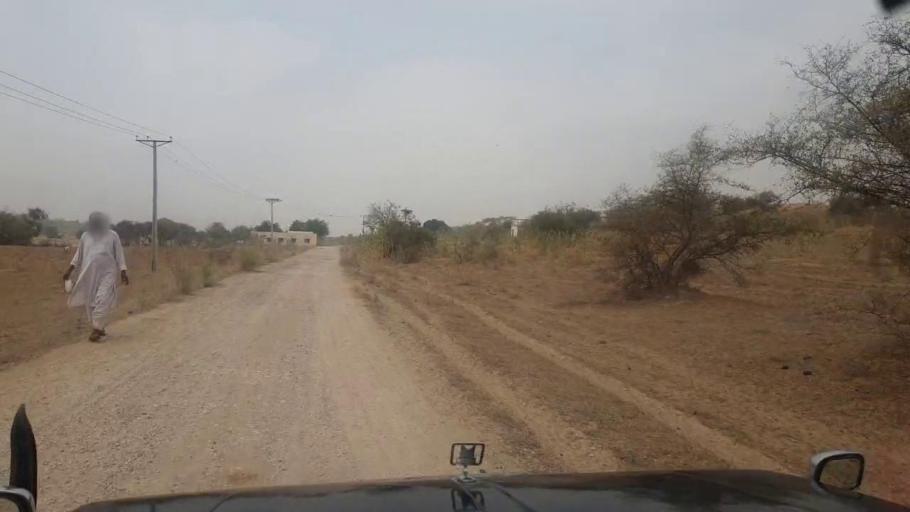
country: PK
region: Sindh
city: Umarkot
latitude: 25.1647
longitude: 70.0618
